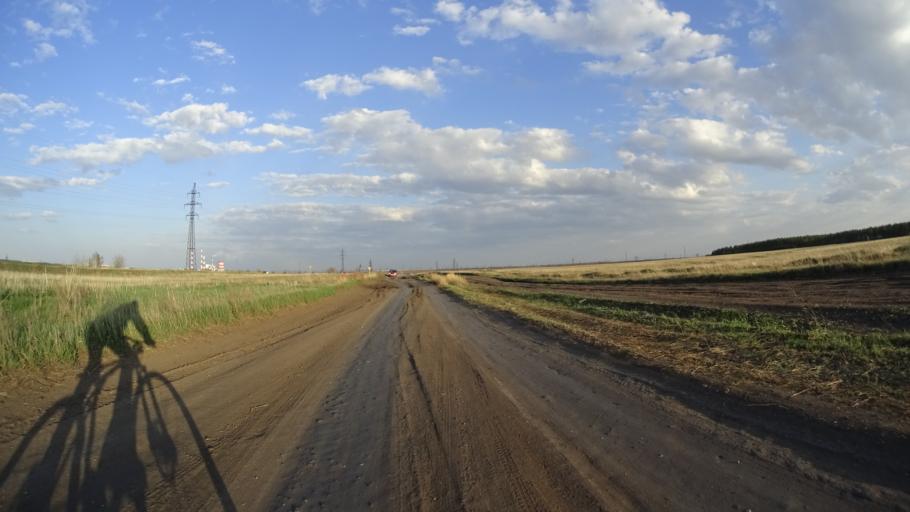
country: RU
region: Chelyabinsk
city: Troitsk
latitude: 54.0510
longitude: 61.5932
